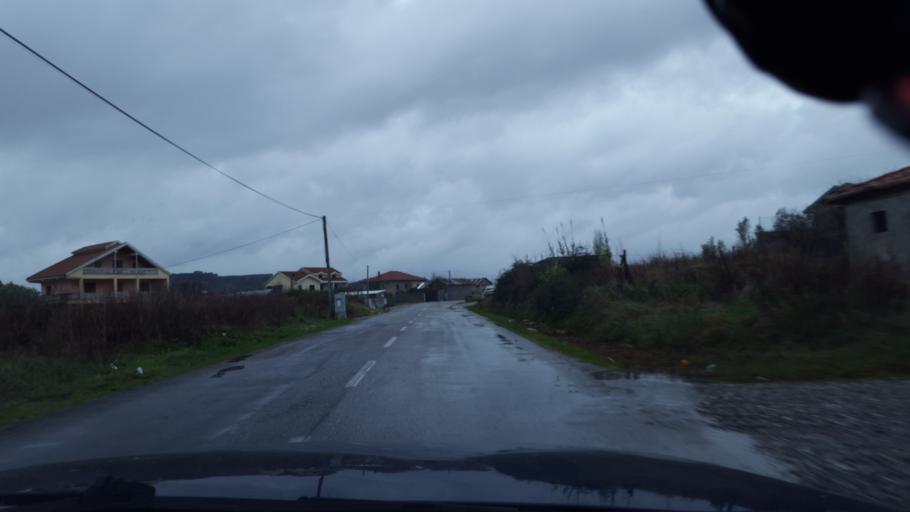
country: AL
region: Shkoder
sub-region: Rrethi i Shkodres
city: Berdica e Madhe
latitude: 42.0277
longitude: 19.4911
